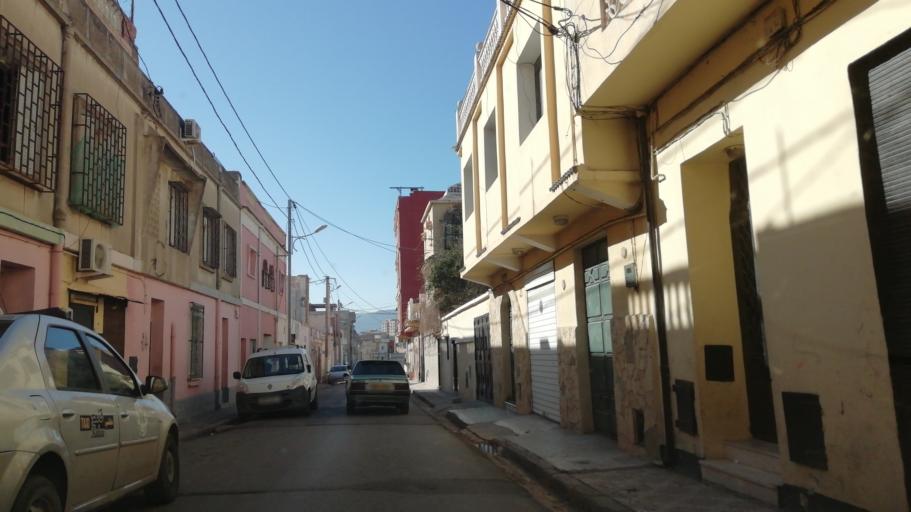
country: DZ
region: Oran
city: Oran
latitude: 35.7042
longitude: -0.6152
